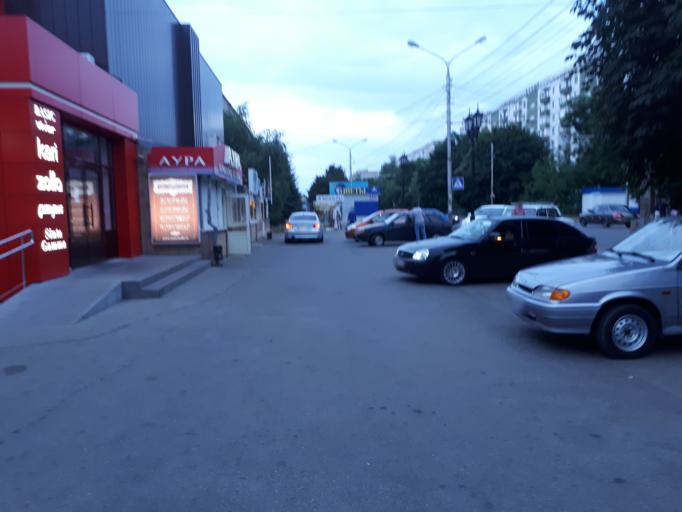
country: RU
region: Stavropol'skiy
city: Stavropol'
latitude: 45.0619
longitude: 41.9241
